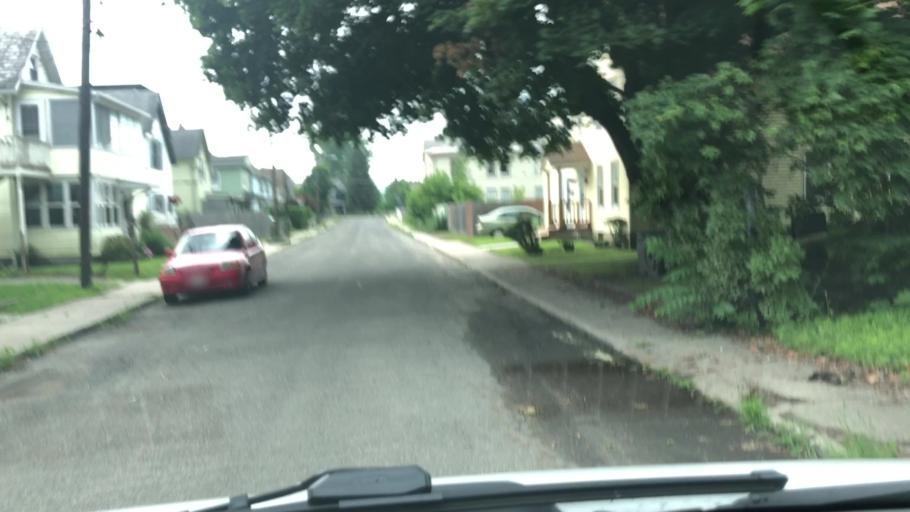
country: US
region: Massachusetts
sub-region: Berkshire County
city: Adams
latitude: 42.6321
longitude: -73.1133
